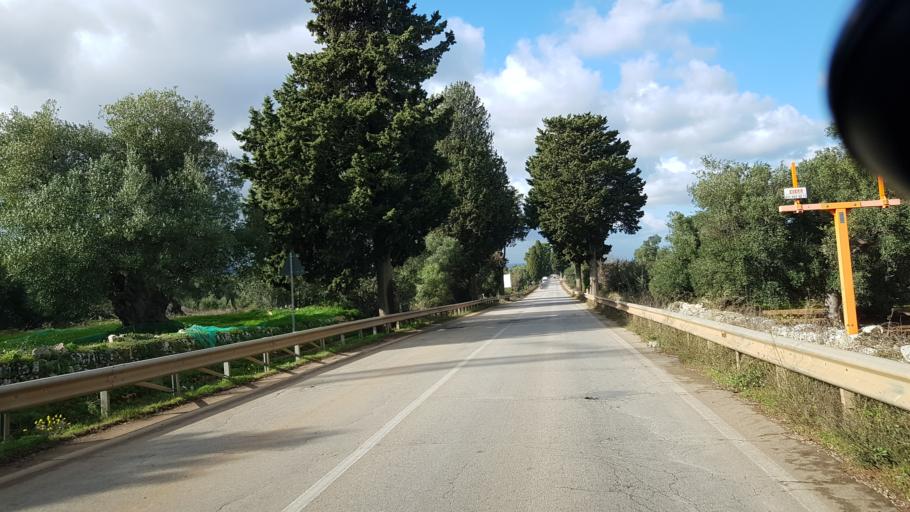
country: IT
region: Apulia
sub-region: Provincia di Brindisi
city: Ostuni
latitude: 40.7531
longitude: 17.5454
